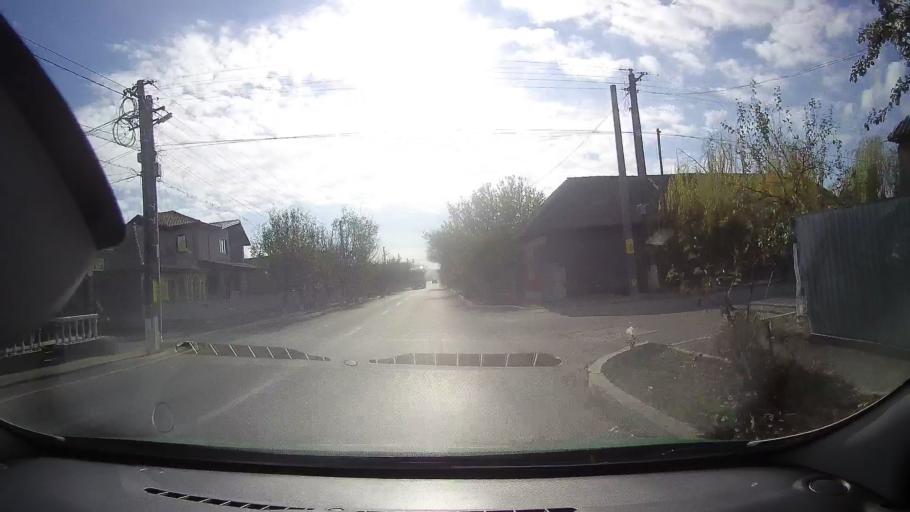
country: RO
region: Tulcea
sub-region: Comuna Sarichioi
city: Sarichioi
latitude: 44.9474
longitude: 28.8525
